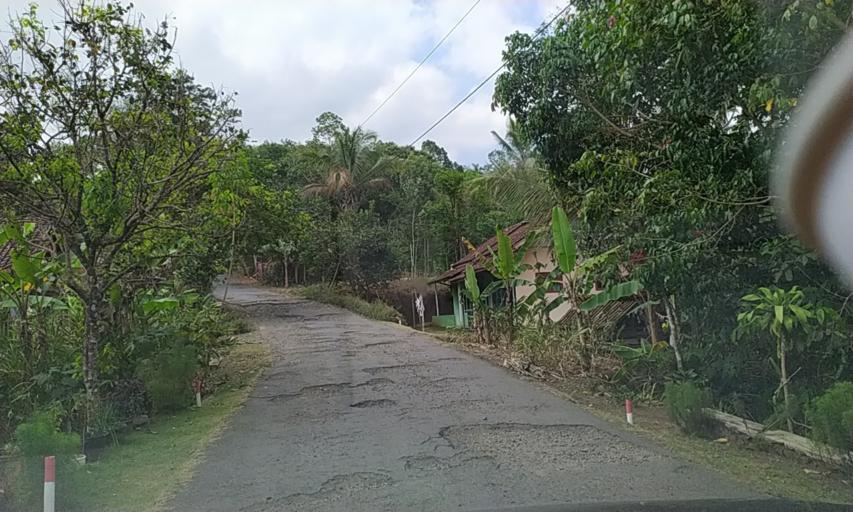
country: ID
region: Central Java
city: Kubang
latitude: -7.2705
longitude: 108.6466
